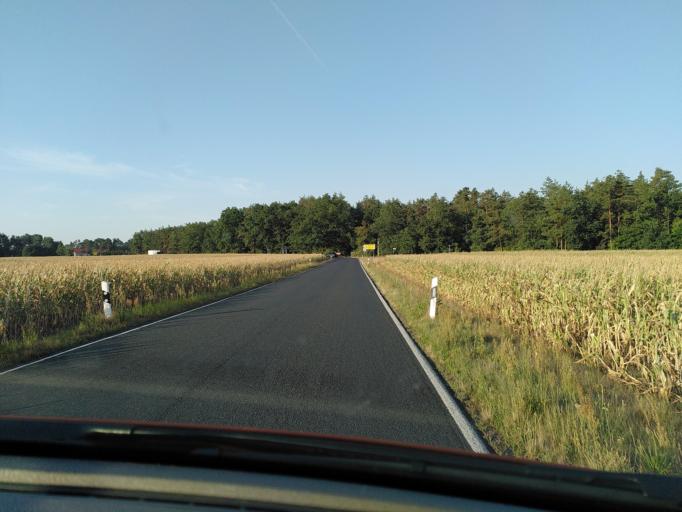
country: DE
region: Saxony
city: Konigswartha
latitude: 51.3045
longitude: 14.3161
